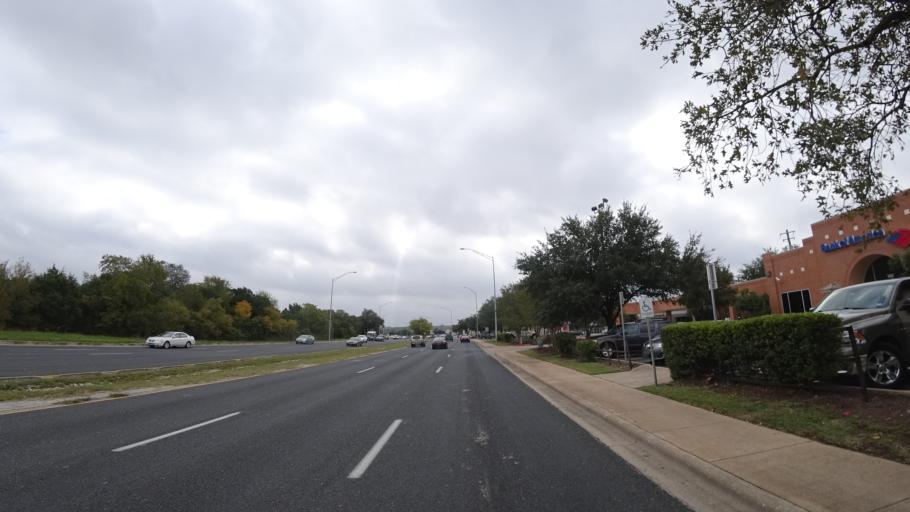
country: US
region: Texas
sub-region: Travis County
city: Shady Hollow
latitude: 30.2166
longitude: -97.8341
